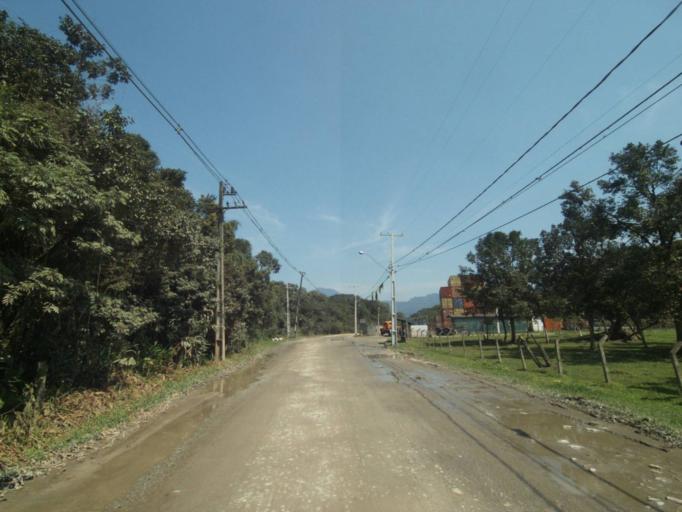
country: BR
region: Parana
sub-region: Paranagua
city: Paranagua
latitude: -25.5526
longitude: -48.5891
